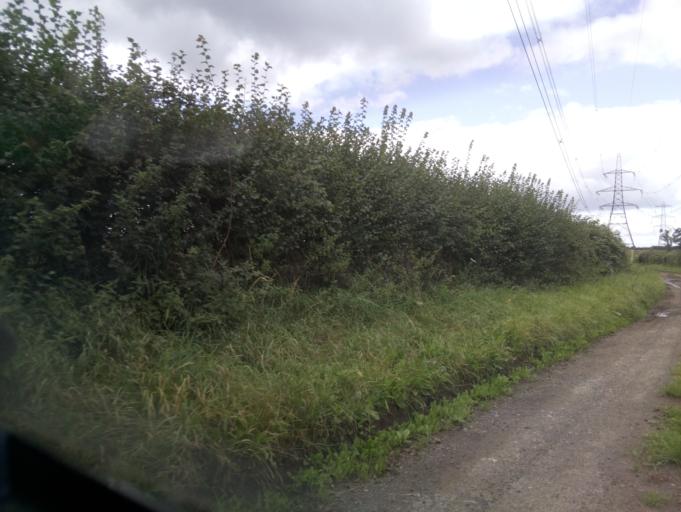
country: GB
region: England
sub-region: Wiltshire
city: Nettleton
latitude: 51.5071
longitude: -2.2233
